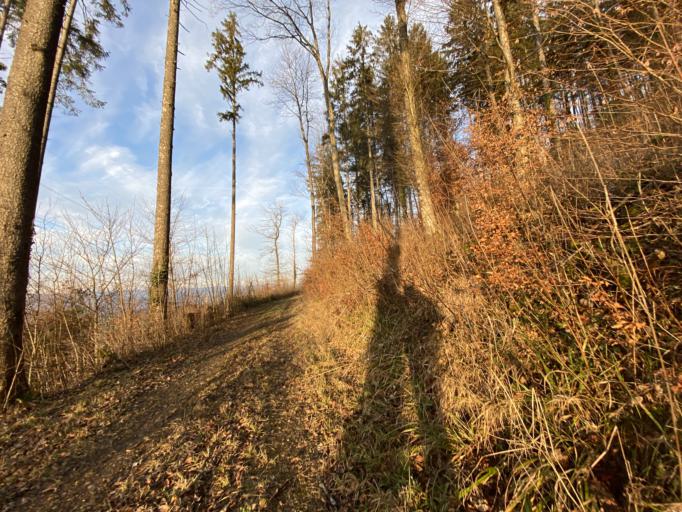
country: CH
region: Aargau
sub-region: Bezirk Laufenburg
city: Frick
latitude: 47.5129
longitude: 8.0382
